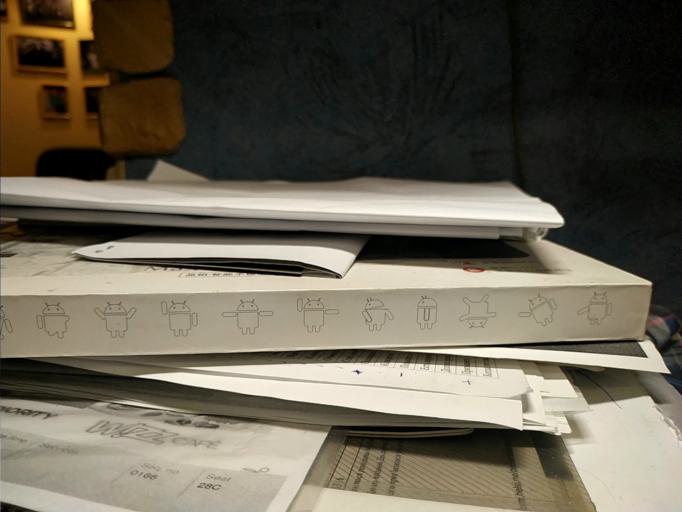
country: RU
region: Tverskaya
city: Zubtsov
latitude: 56.0788
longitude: 34.8105
